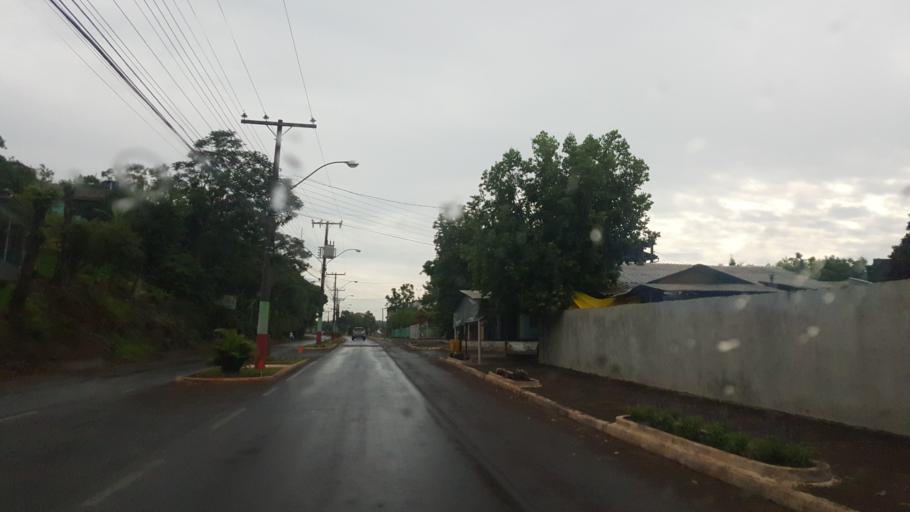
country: BR
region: Rio Grande do Sul
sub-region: Frederico Westphalen
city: Frederico Westphalen
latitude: -27.1004
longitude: -53.3919
